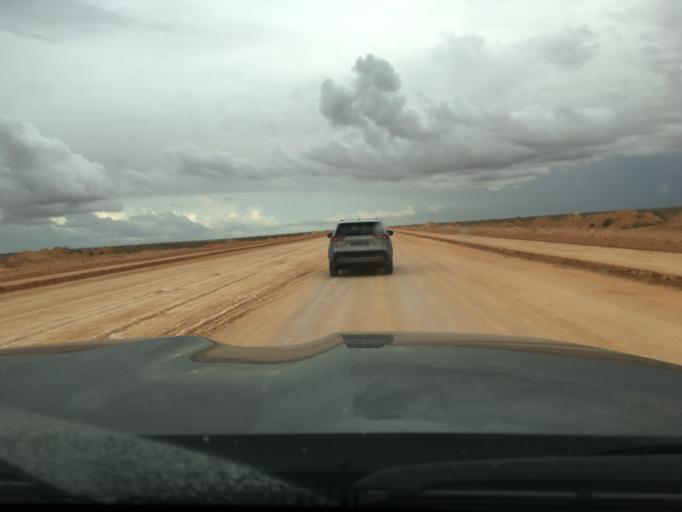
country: TN
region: Madanin
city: Medenine
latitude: 33.2762
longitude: 10.5913
